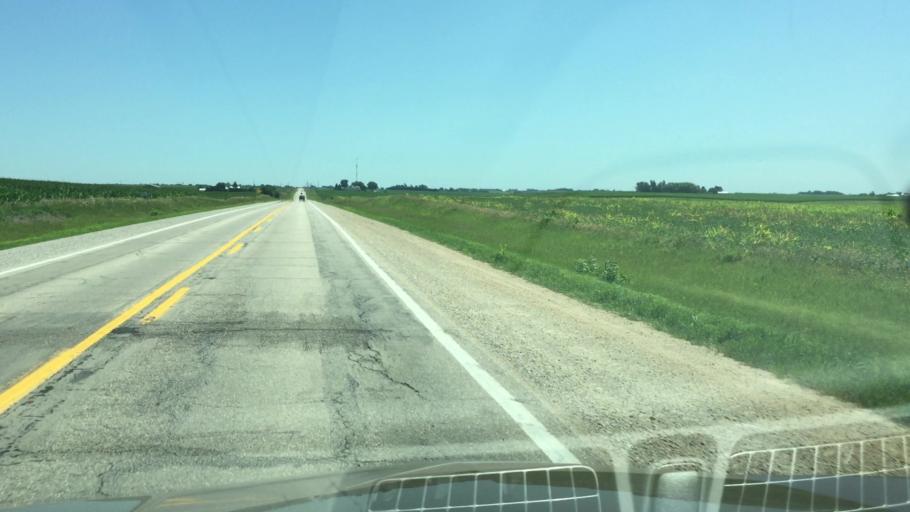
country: US
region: Iowa
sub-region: Cedar County
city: Mechanicsville
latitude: 41.8888
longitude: -91.2098
